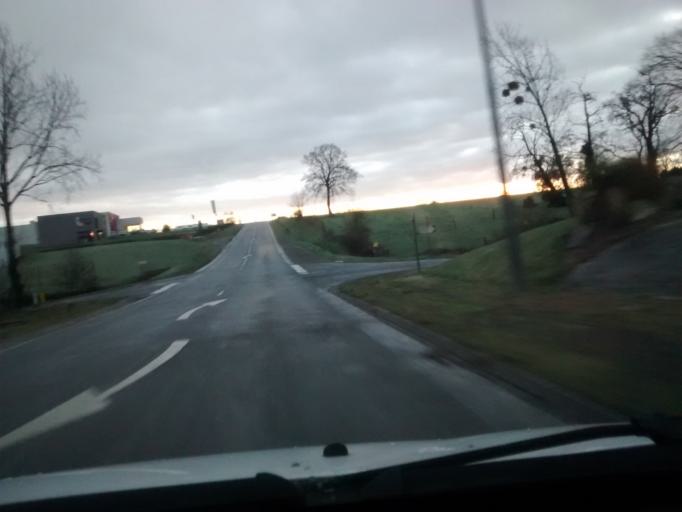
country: FR
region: Brittany
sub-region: Departement d'Ille-et-Vilaine
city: Chateaubourg
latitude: 48.1002
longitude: -1.4085
